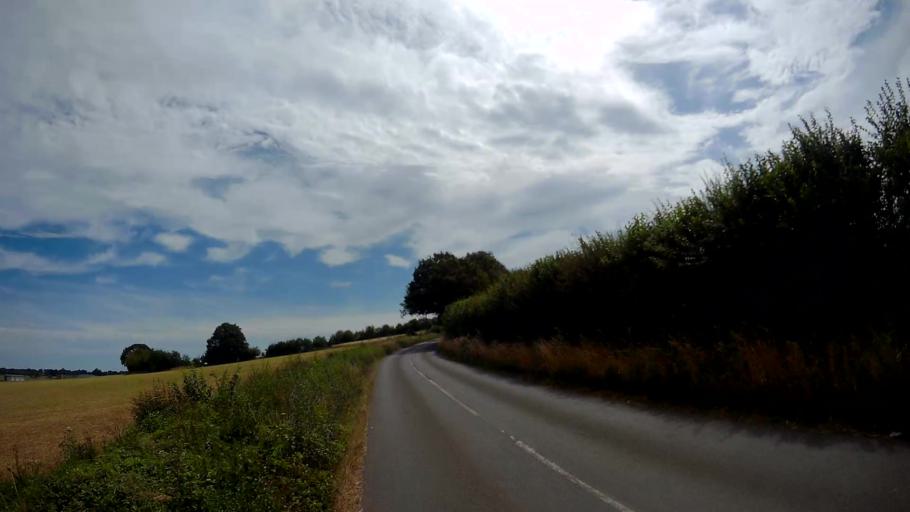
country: GB
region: England
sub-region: Hampshire
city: Long Sutton
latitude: 51.2286
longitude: -0.9579
